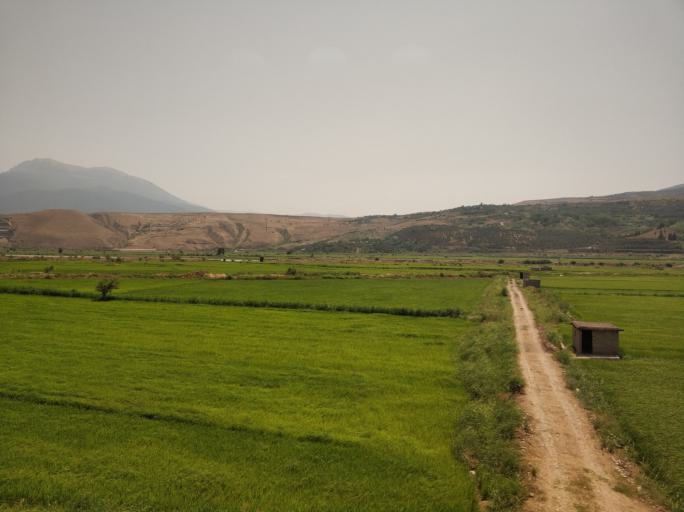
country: IR
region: Gilan
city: Pa'in-e Bazar-e Rudbar
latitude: 36.8797
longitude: 49.4968
